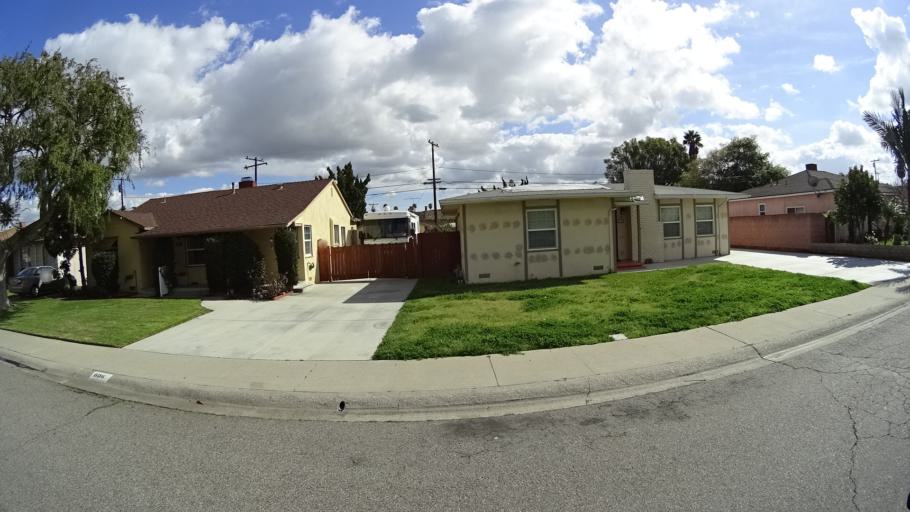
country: US
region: California
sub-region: Orange County
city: Anaheim
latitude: 33.8448
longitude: -117.8998
